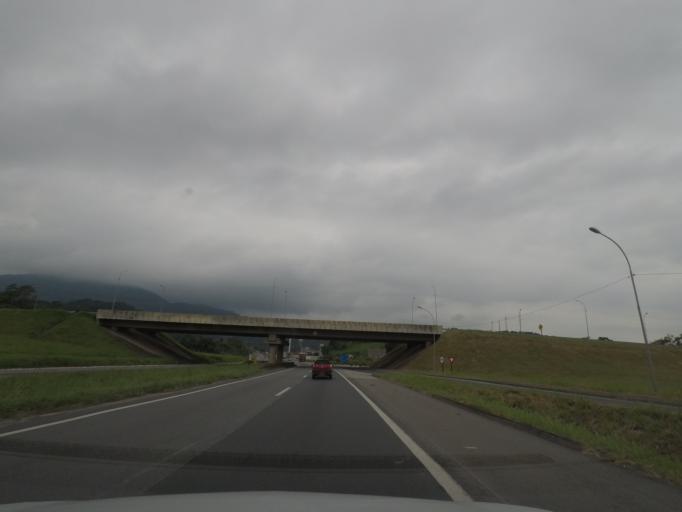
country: BR
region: Sao Paulo
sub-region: Miracatu
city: Miracatu
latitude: -24.2540
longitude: -47.3752
